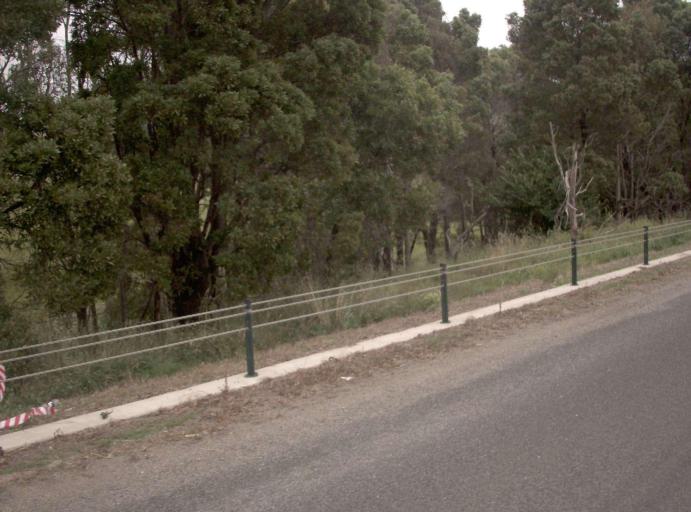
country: AU
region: Victoria
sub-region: Baw Baw
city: Warragul
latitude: -38.1825
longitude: 145.9891
